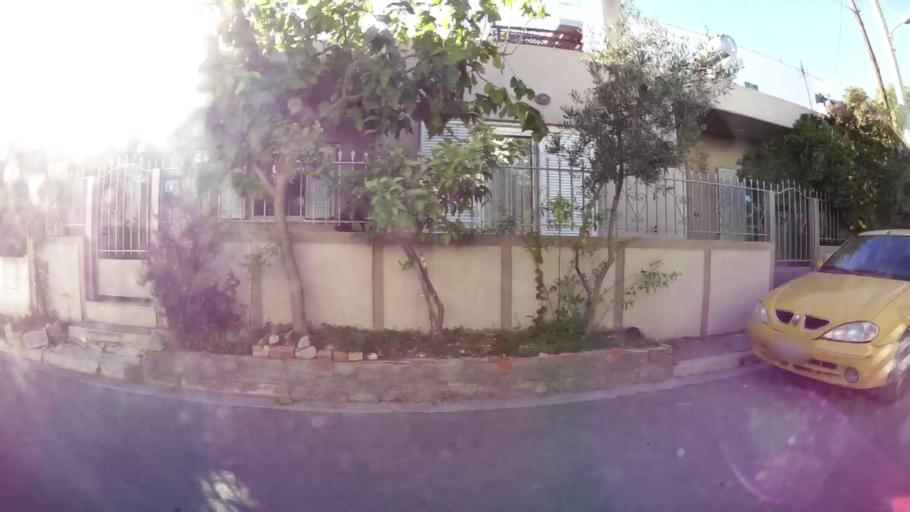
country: GR
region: Attica
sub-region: Nomarchia Anatolikis Attikis
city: Acharnes
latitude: 38.0942
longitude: 23.7370
